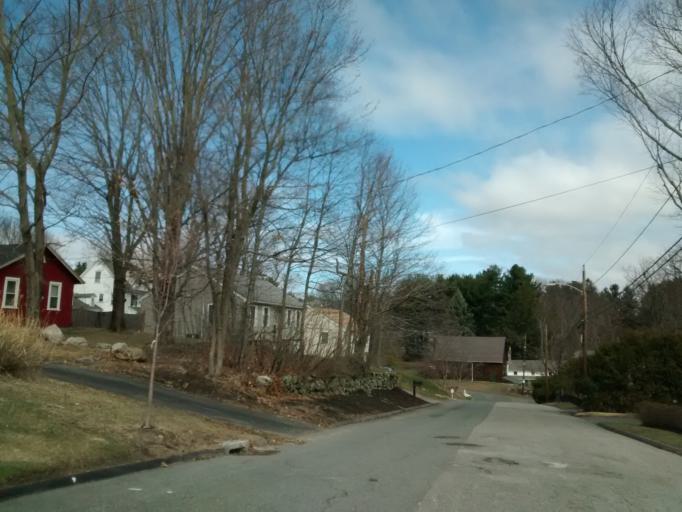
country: US
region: Massachusetts
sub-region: Worcester County
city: Worcester
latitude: 42.2954
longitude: -71.8198
